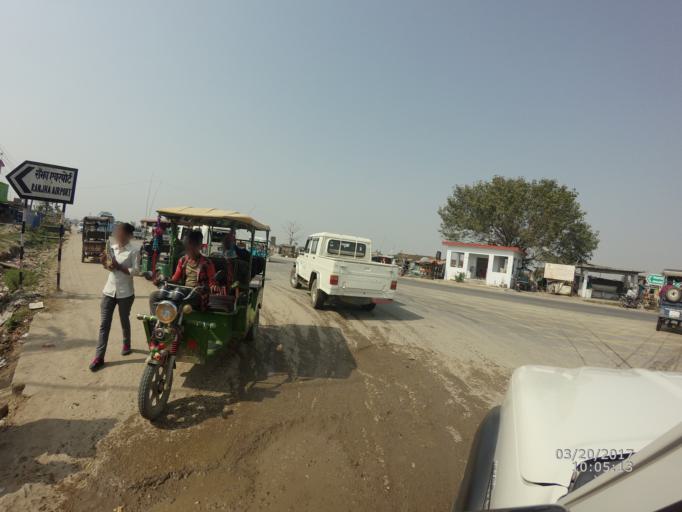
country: NP
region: Mid Western
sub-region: Bheri Zone
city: Nepalgunj
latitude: 28.1011
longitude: 81.6540
